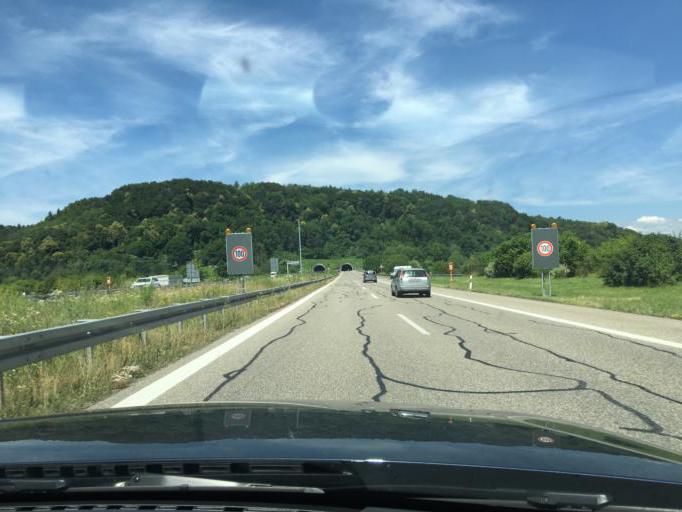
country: DE
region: Baden-Wuerttemberg
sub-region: Freiburg Region
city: Rheinfelden (Baden)
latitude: 47.5665
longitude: 7.7599
